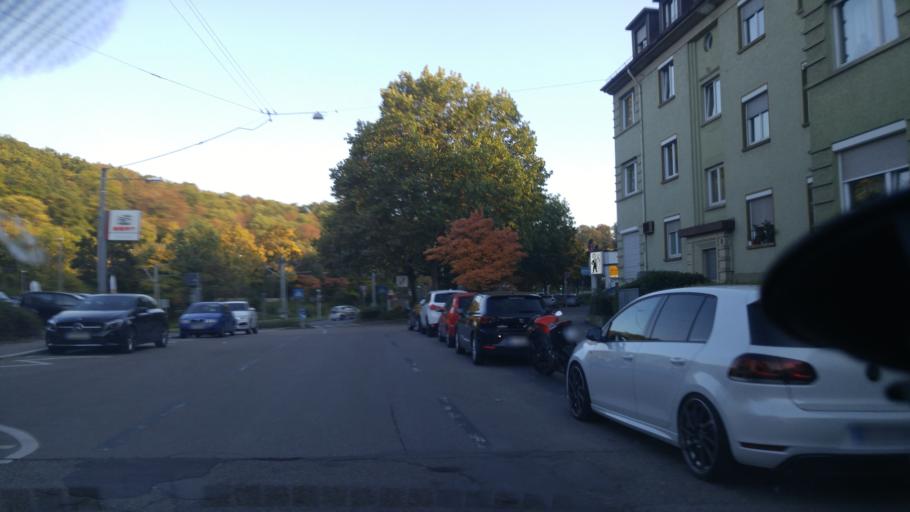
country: DE
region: Baden-Wuerttemberg
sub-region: Regierungsbezirk Stuttgart
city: Stuttgart Feuerbach
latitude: 48.7772
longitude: 9.1322
